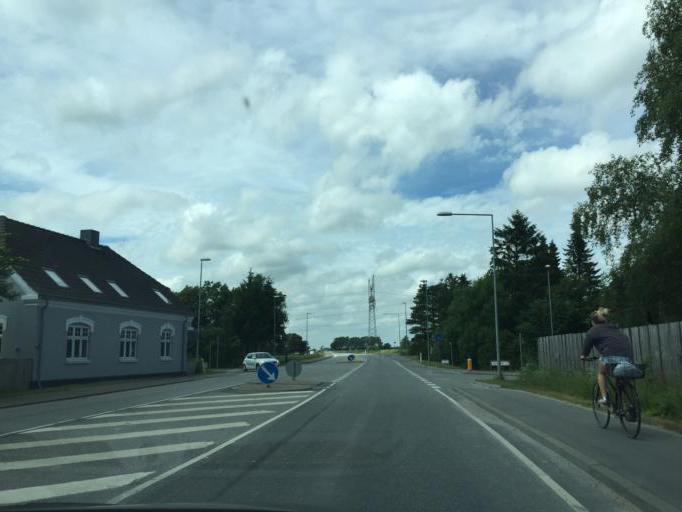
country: DK
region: South Denmark
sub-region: Odense Kommune
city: Hojby
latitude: 55.3313
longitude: 10.3929
